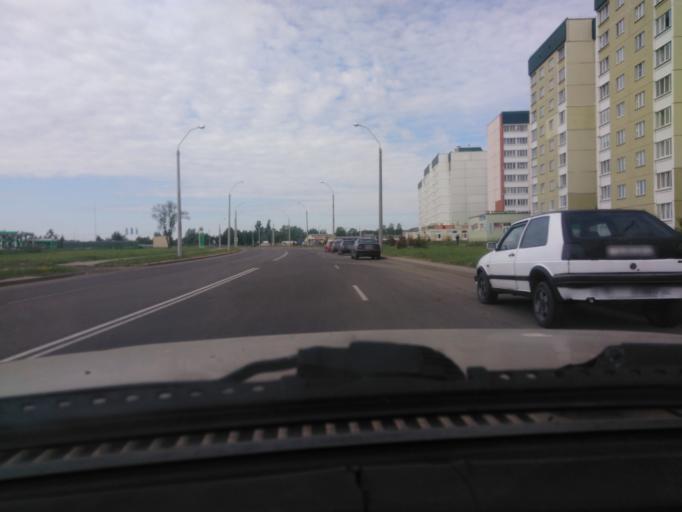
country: BY
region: Mogilev
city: Mahilyow
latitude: 53.9136
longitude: 30.2863
